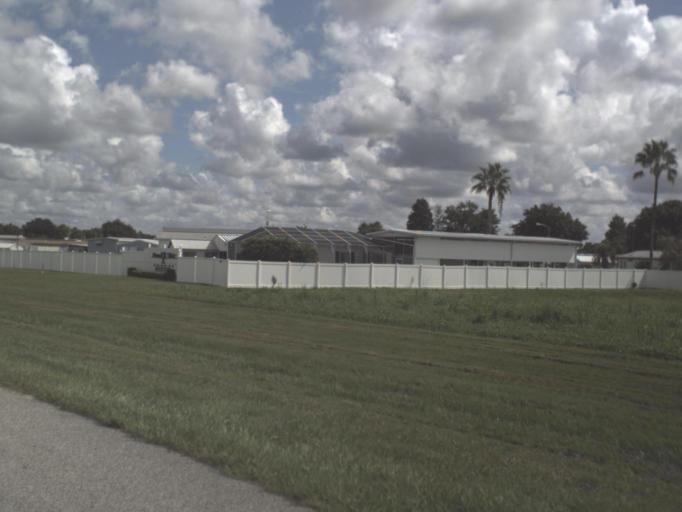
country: US
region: Florida
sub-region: Polk County
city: Polk City
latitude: 28.1629
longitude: -81.8576
